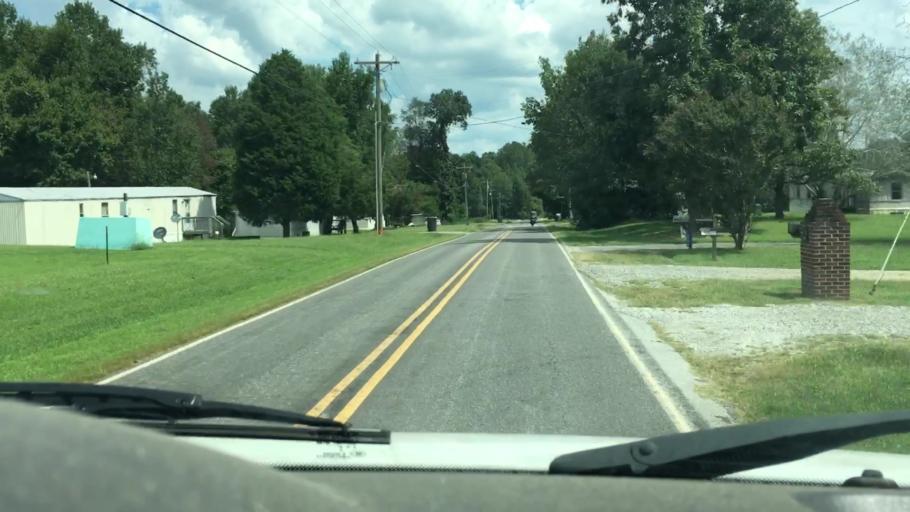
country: US
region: North Carolina
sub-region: Iredell County
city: Mooresville
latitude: 35.6679
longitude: -80.7885
